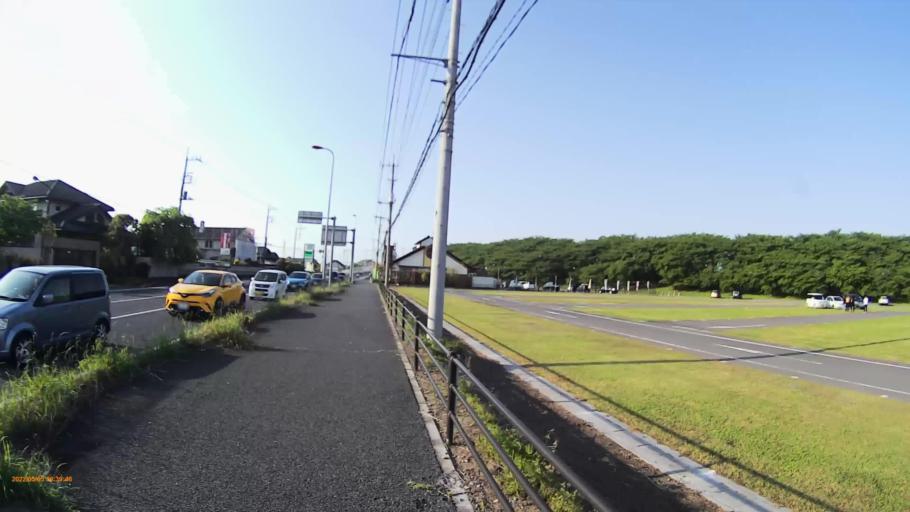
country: JP
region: Saitama
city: Satte
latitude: 36.0927
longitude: 139.7208
